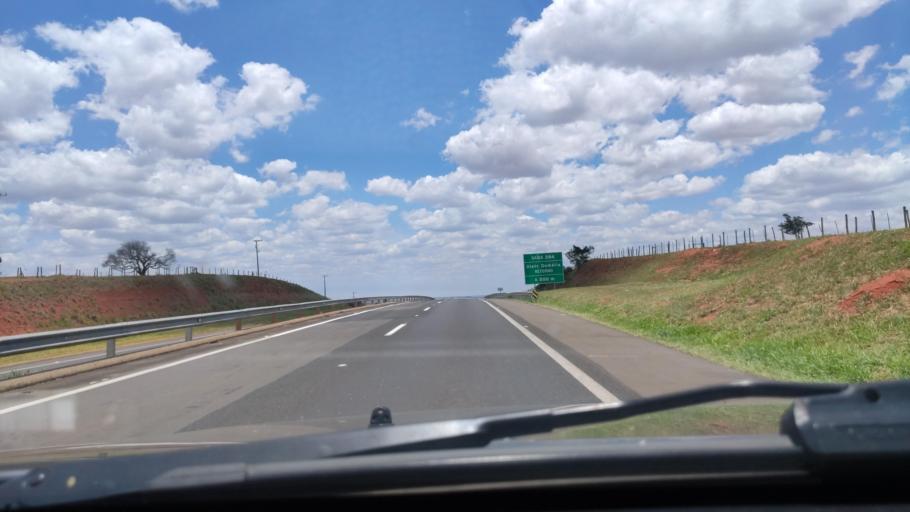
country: BR
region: Sao Paulo
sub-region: Duartina
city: Duartina
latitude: -22.6226
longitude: -49.3832
